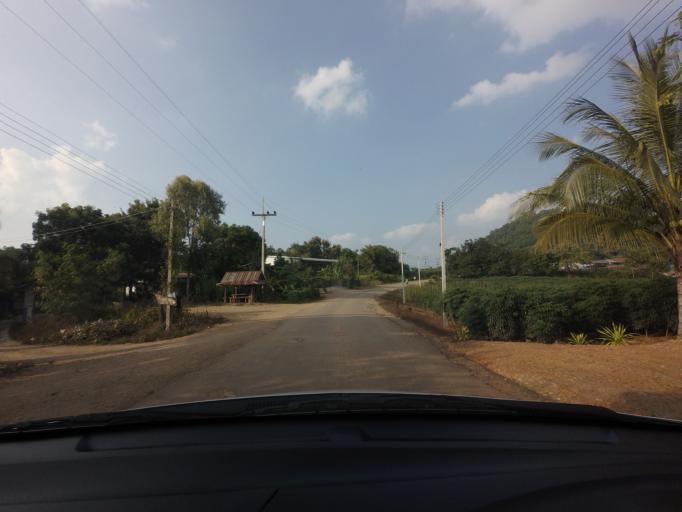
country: TH
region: Nakhon Ratchasima
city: Pak Chong
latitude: 14.5278
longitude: 101.5746
